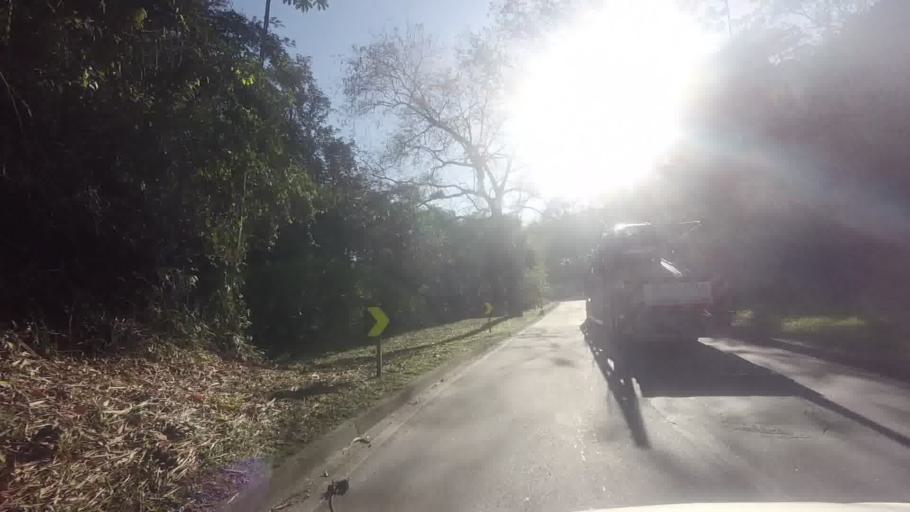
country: BR
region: Rio de Janeiro
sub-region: Petropolis
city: Petropolis
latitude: -22.5944
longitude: -43.2793
